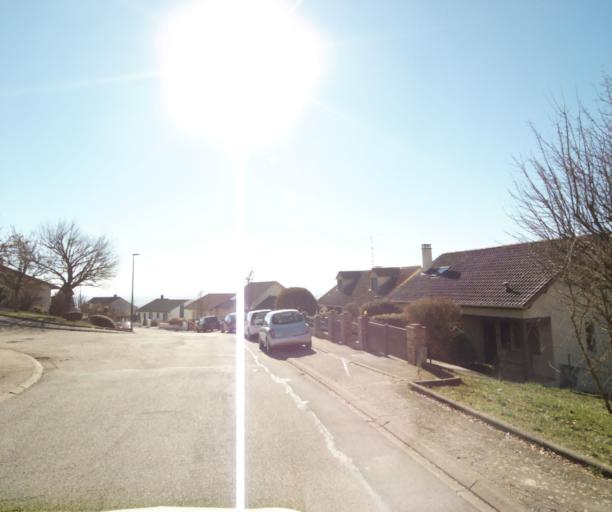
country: FR
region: Lorraine
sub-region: Departement de Meurthe-et-Moselle
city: Essey-les-Nancy
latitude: 48.7135
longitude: 6.2215
